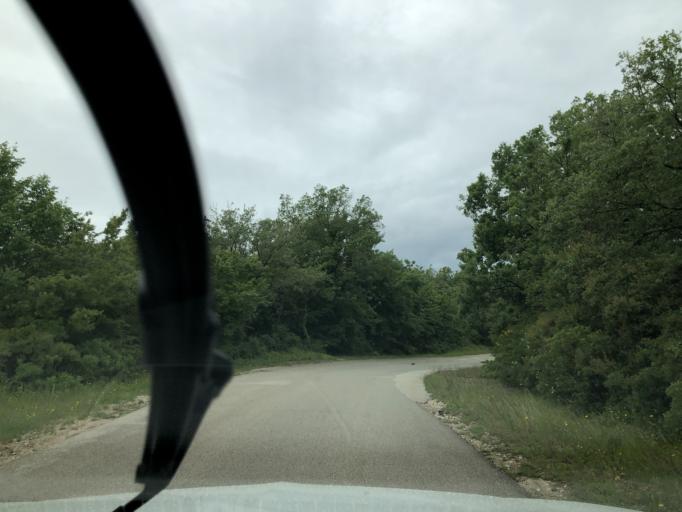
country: HR
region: Istarska
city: Buje
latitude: 45.4371
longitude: 13.6665
